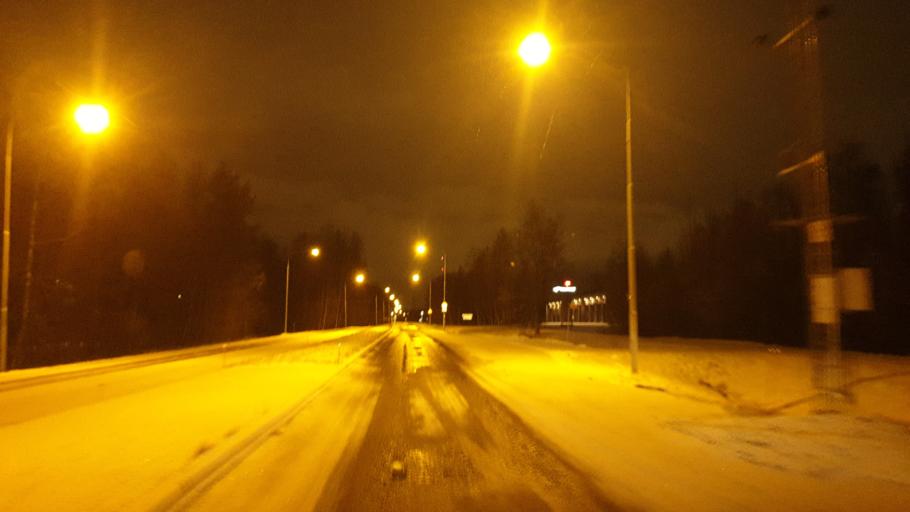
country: FI
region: Northern Ostrobothnia
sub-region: Oulu
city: Oulu
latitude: 64.9745
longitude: 25.4884
